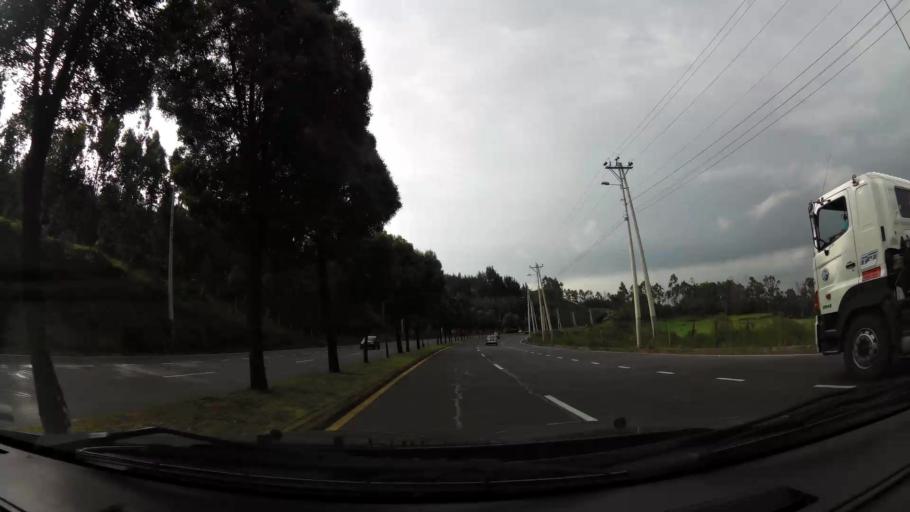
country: EC
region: Pichincha
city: Sangolqui
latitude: -0.3460
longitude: -78.5237
